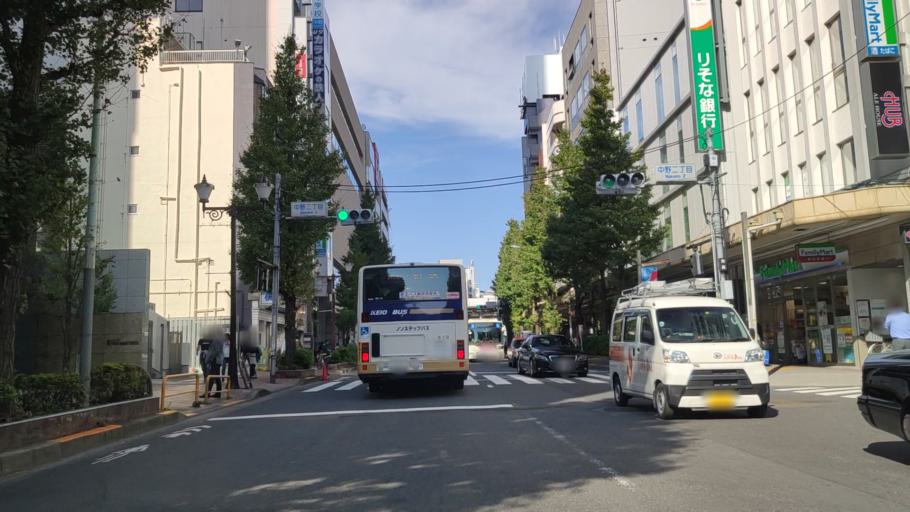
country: JP
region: Tokyo
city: Tokyo
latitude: 35.7039
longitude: 139.6655
